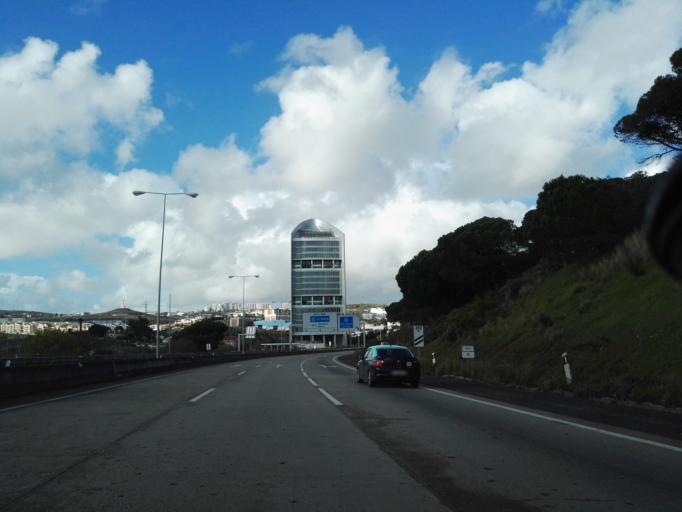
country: PT
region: Lisbon
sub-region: Oeiras
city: Alges
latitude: 38.7122
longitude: -9.2223
